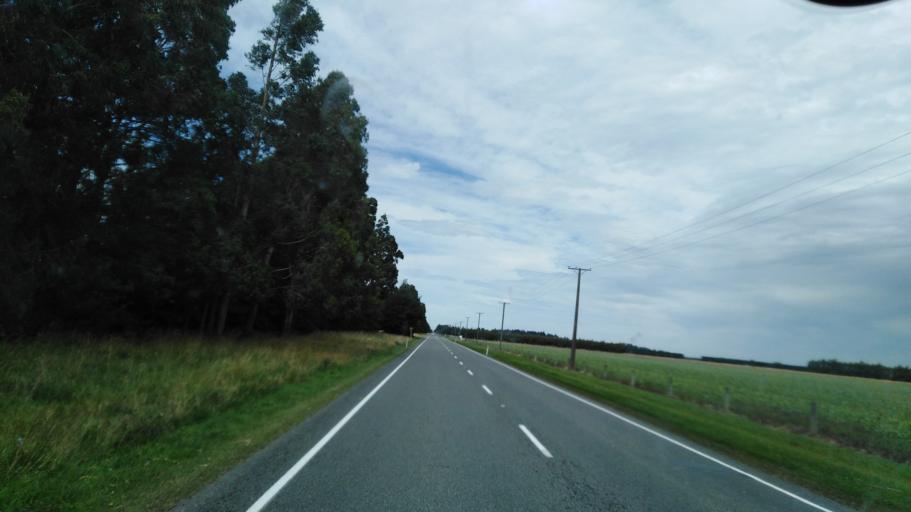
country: NZ
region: Canterbury
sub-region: Selwyn District
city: Darfield
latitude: -43.4216
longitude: 172.0504
